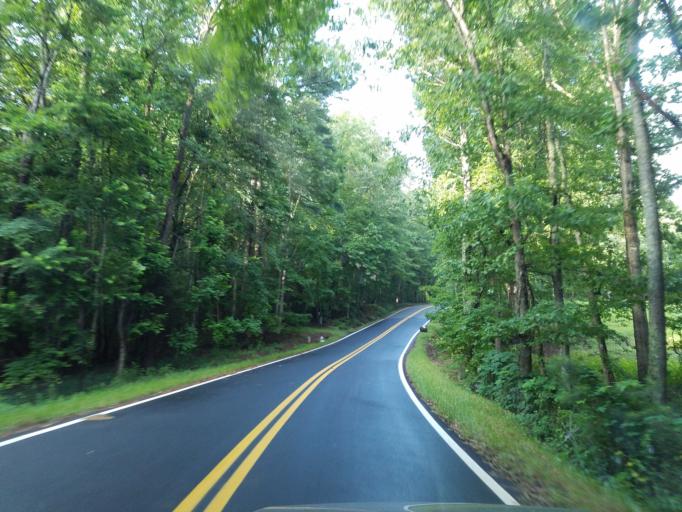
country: US
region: Georgia
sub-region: Bartow County
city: Rydal
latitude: 34.2263
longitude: -84.6316
